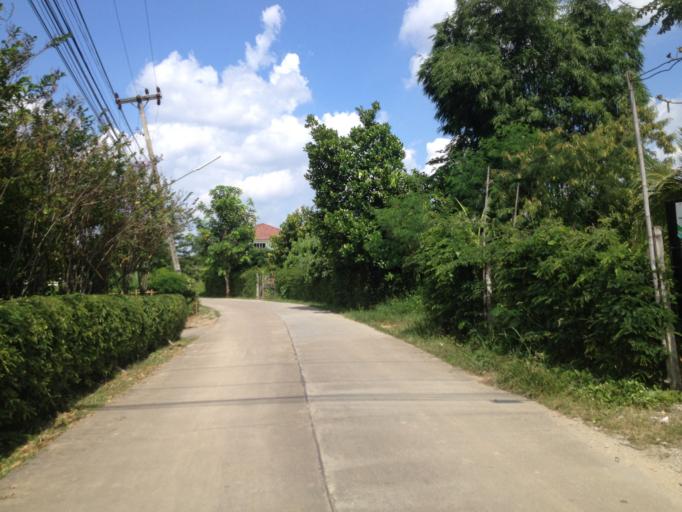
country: TH
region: Chiang Mai
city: Hang Dong
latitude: 18.7213
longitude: 98.9201
